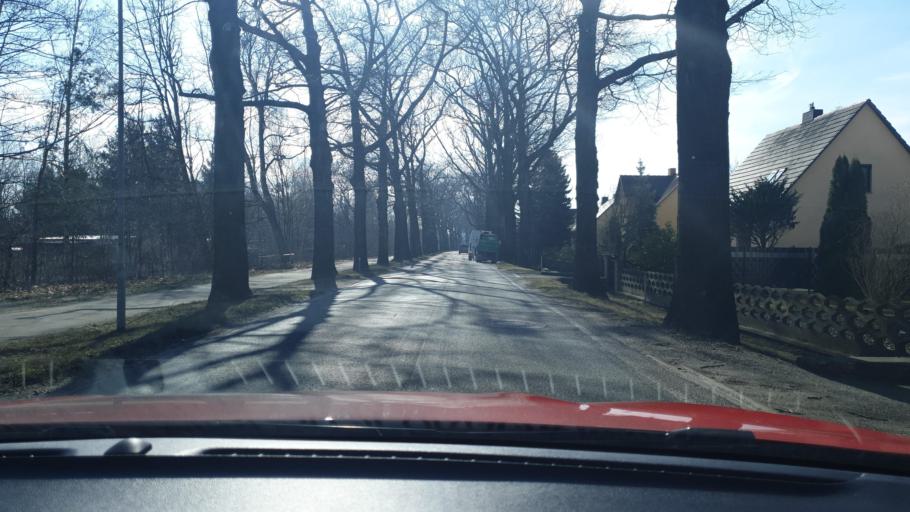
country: DE
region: Saxony
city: Ossling
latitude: 51.4495
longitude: 14.1336
